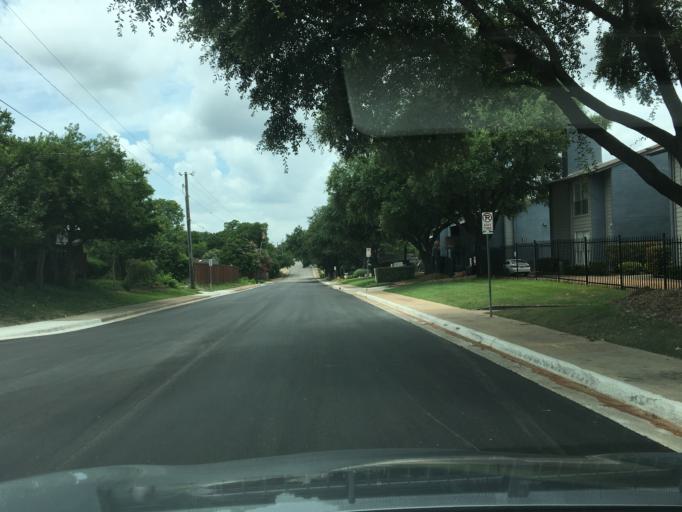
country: US
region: Texas
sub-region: Dallas County
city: Richardson
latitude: 32.9168
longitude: -96.7143
